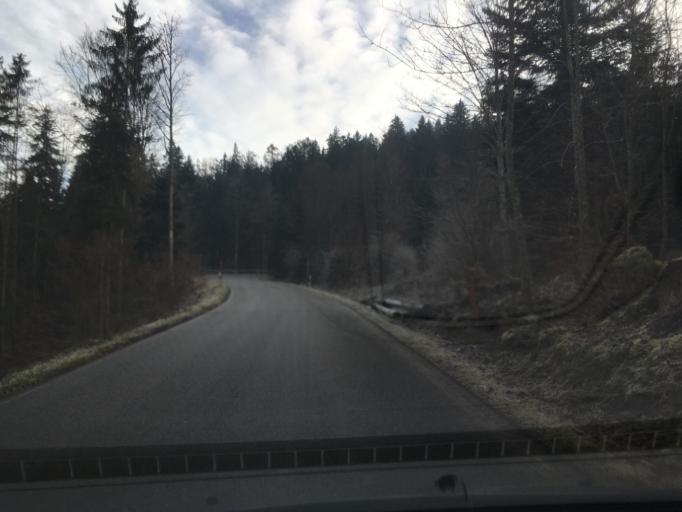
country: DE
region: Baden-Wuerttemberg
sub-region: Freiburg Region
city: Hausern
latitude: 47.7468
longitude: 8.1892
